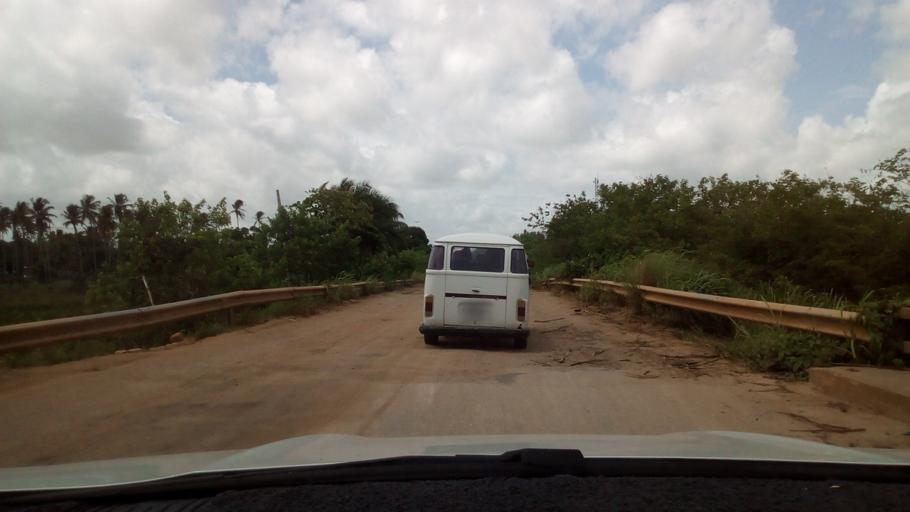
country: BR
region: Paraiba
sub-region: Alhandra
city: Alhandra
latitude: -7.4628
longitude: -34.9172
